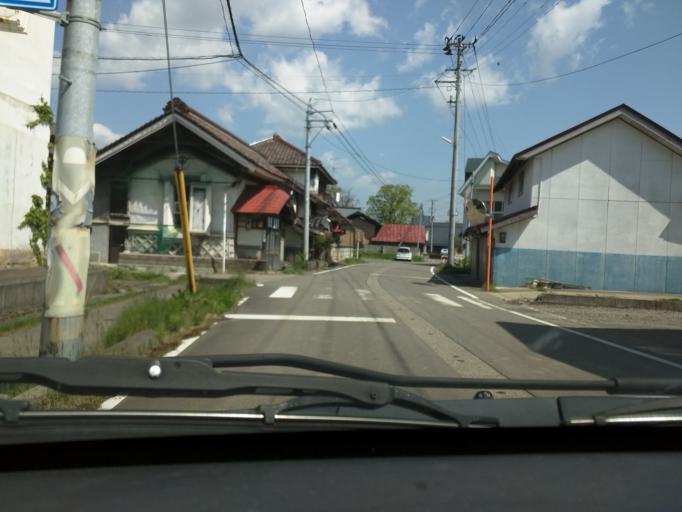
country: JP
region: Fukushima
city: Kitakata
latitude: 37.5885
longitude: 139.8353
